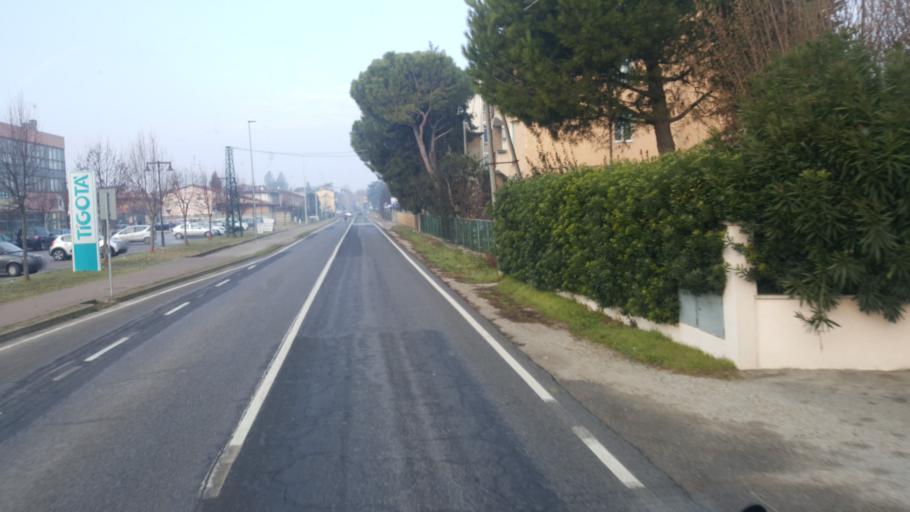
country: IT
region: Emilia-Romagna
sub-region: Provincia di Ravenna
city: Bagnacavallo
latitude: 44.4124
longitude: 11.9873
